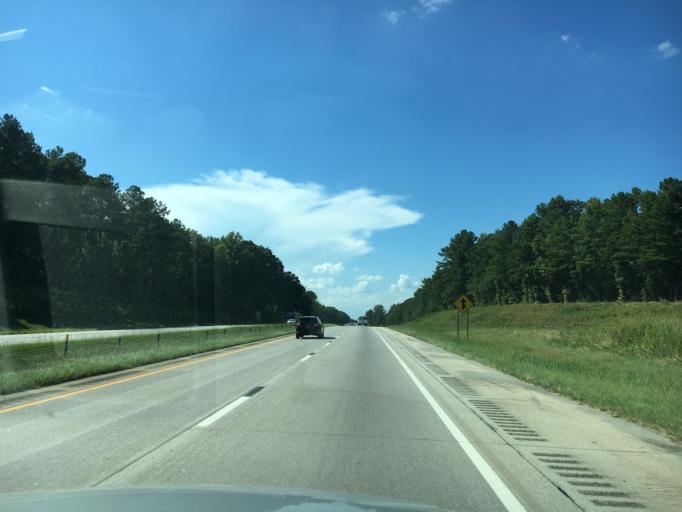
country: US
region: South Carolina
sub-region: Laurens County
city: Watts Mills
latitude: 34.5694
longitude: -82.0298
